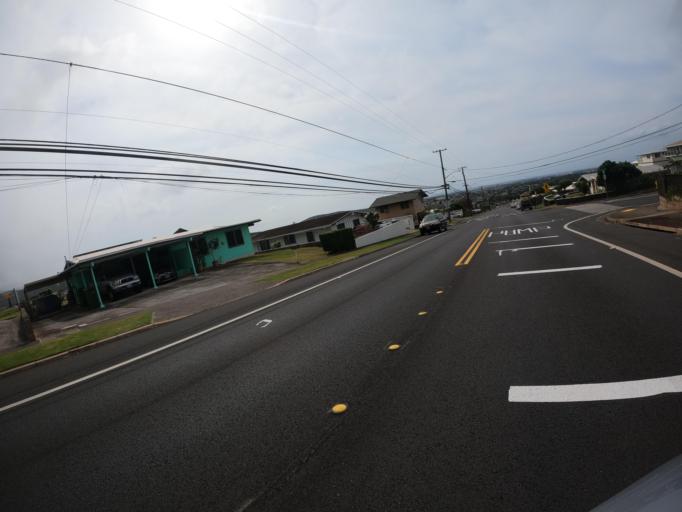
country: US
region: Hawaii
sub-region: Honolulu County
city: Halawa Heights
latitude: 21.3790
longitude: -157.9155
